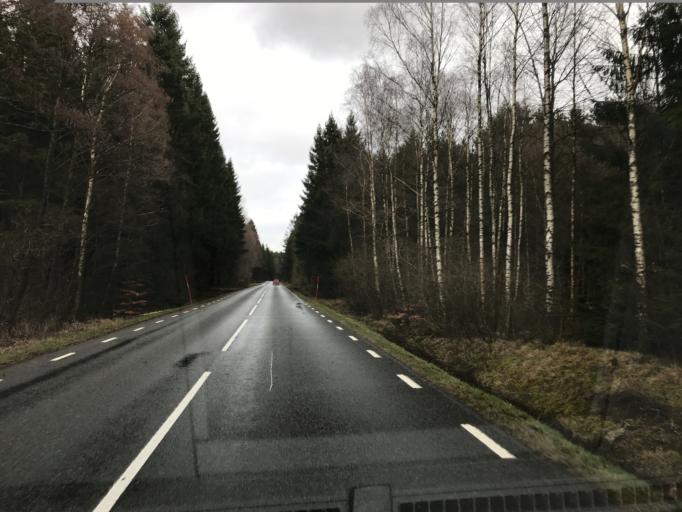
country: SE
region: Skane
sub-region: Hassleholms Kommun
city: Tormestorp
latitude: 56.0796
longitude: 13.7734
